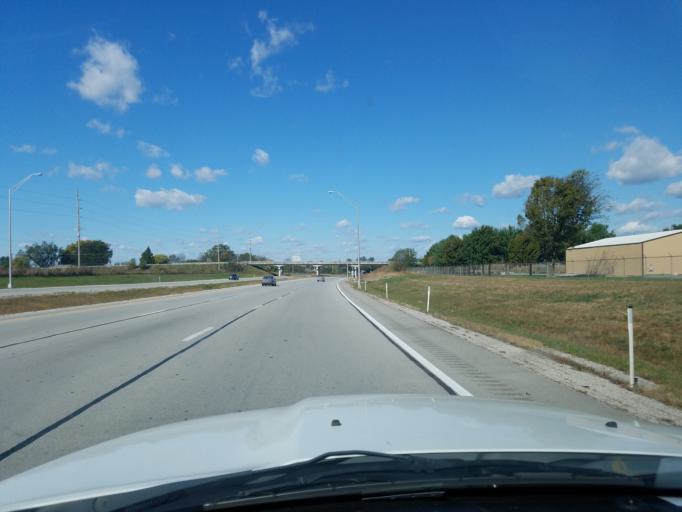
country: US
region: Kentucky
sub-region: Warren County
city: Plano
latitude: 36.9129
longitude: -86.4377
